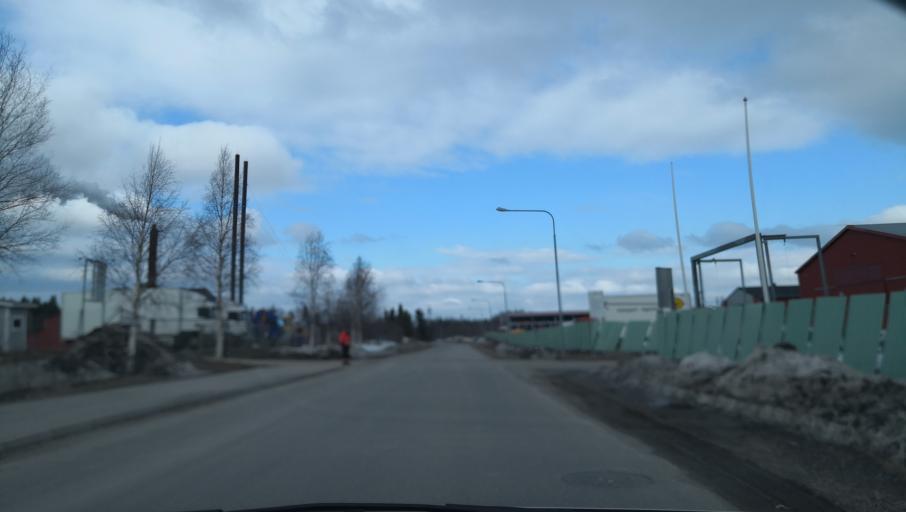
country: SE
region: Vaesterbotten
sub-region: Vannas Kommun
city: Vaennaes
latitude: 63.9147
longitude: 19.7438
